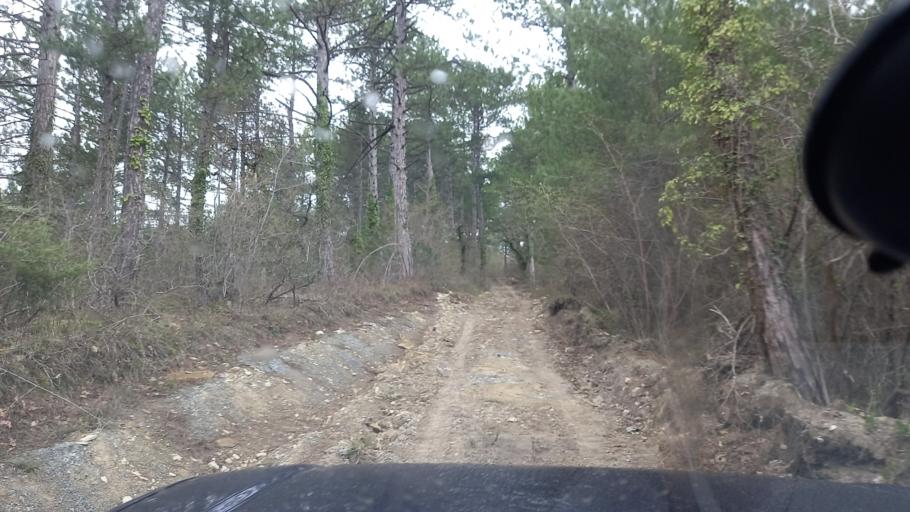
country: RU
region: Krasnodarskiy
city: Arkhipo-Osipovka
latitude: 44.3727
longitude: 38.4731
